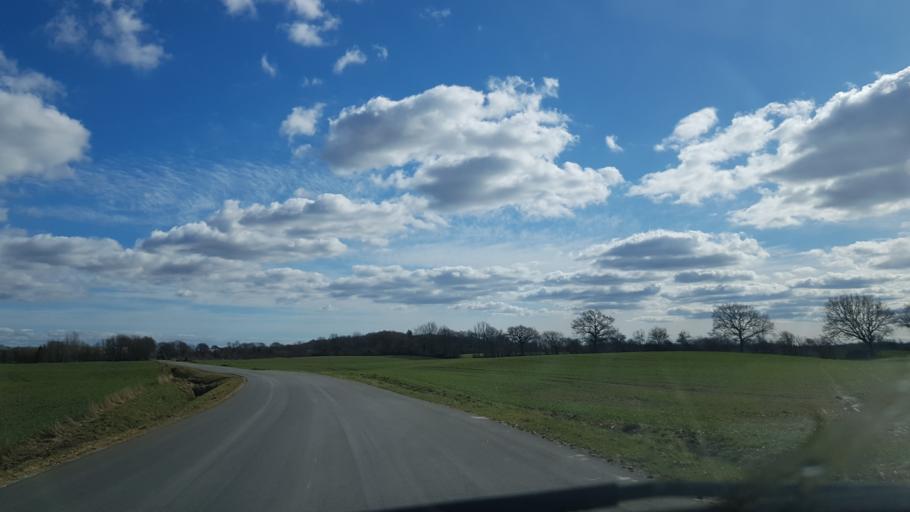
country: DK
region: South Denmark
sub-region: Kolding Kommune
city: Vamdrup
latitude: 55.3703
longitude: 9.3085
